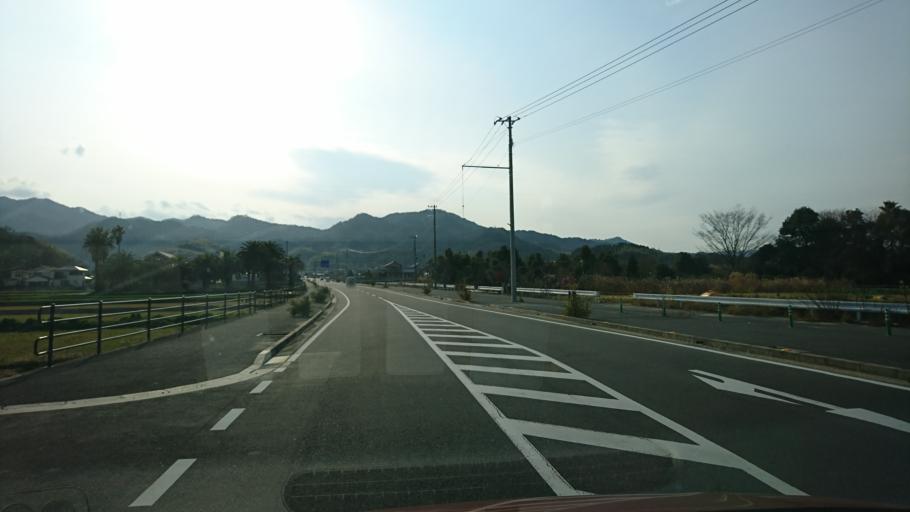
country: JP
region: Ehime
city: Saijo
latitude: 34.0224
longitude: 132.9954
